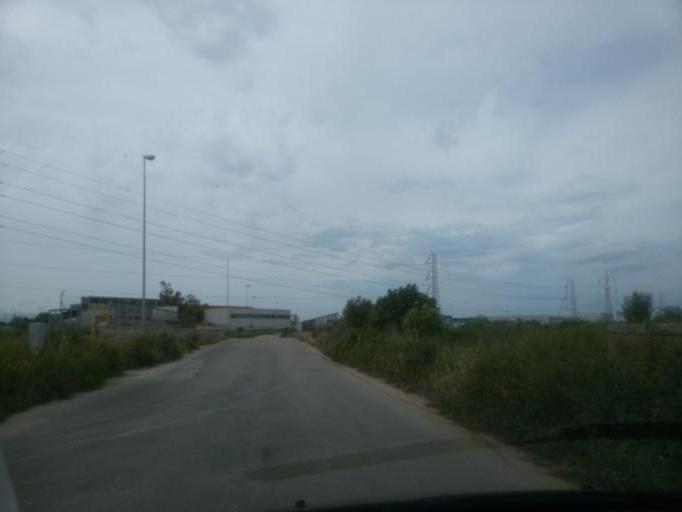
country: IT
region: Apulia
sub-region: Provincia di Brindisi
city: La Rosa
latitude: 40.6260
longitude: 17.9830
